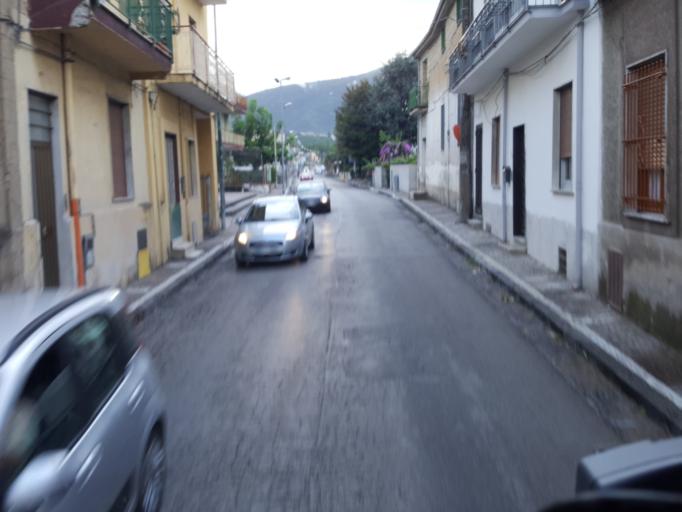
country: IT
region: Campania
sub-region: Provincia di Napoli
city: Palma Campania
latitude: 40.8796
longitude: 14.5536
